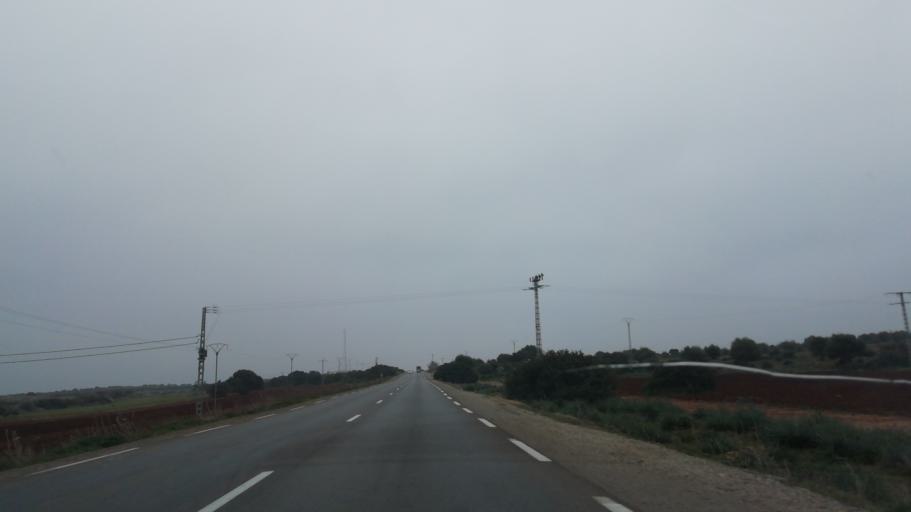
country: DZ
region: Mascara
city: Mascara
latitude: 35.3056
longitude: 0.4263
